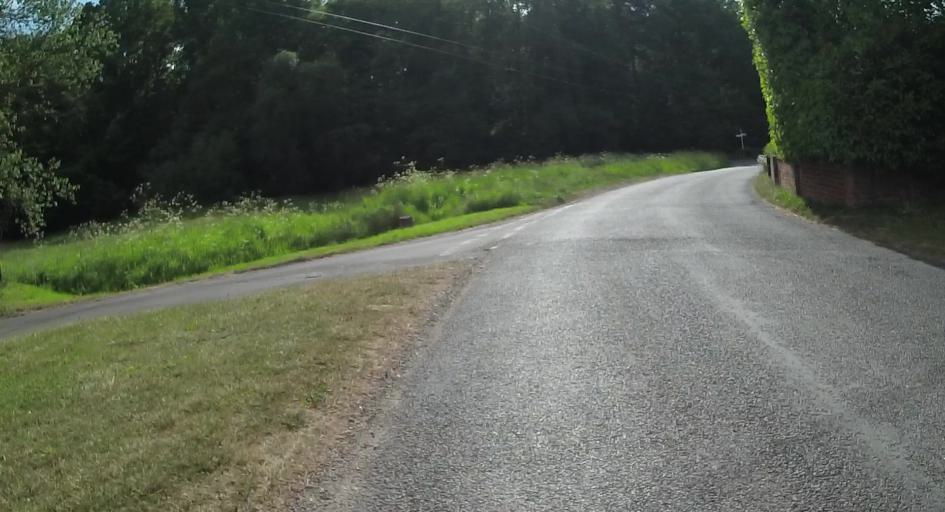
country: GB
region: England
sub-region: Hampshire
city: Hook
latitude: 51.3172
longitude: -0.9455
